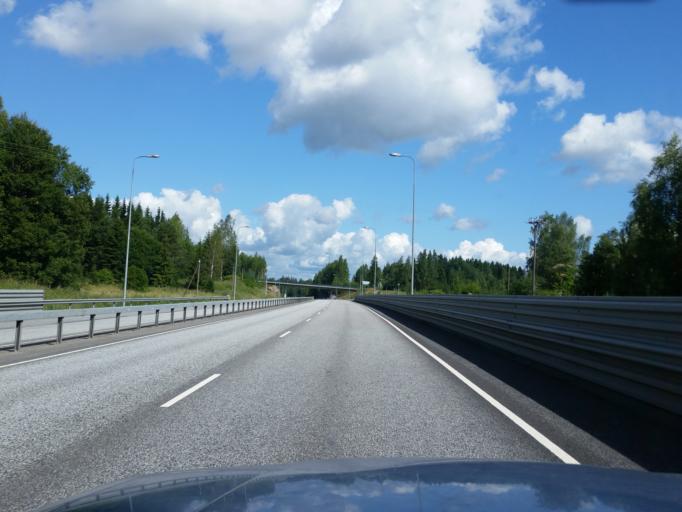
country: FI
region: Uusimaa
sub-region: Helsinki
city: Vihti
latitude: 60.3125
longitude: 24.3486
